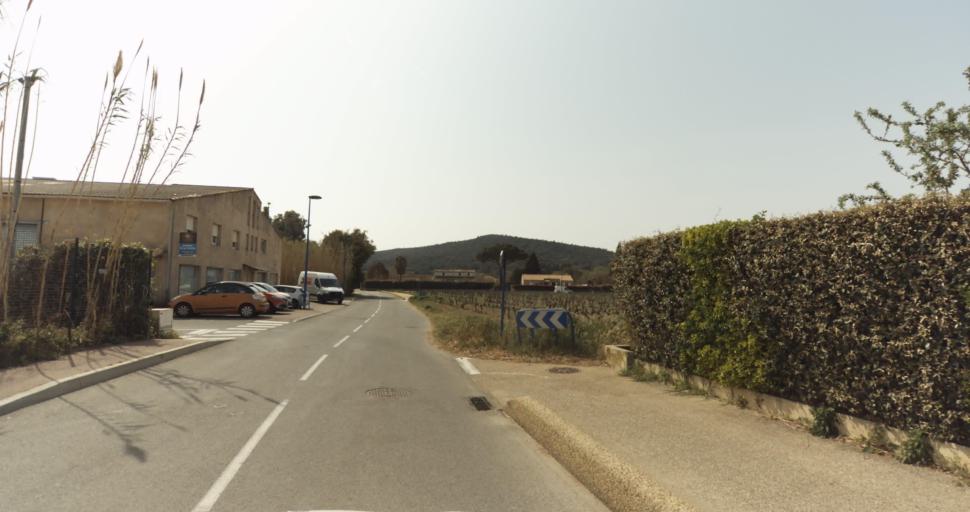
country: FR
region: Provence-Alpes-Cote d'Azur
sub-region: Departement du Var
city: Bormes-les-Mimosas
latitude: 43.1336
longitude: 6.3465
